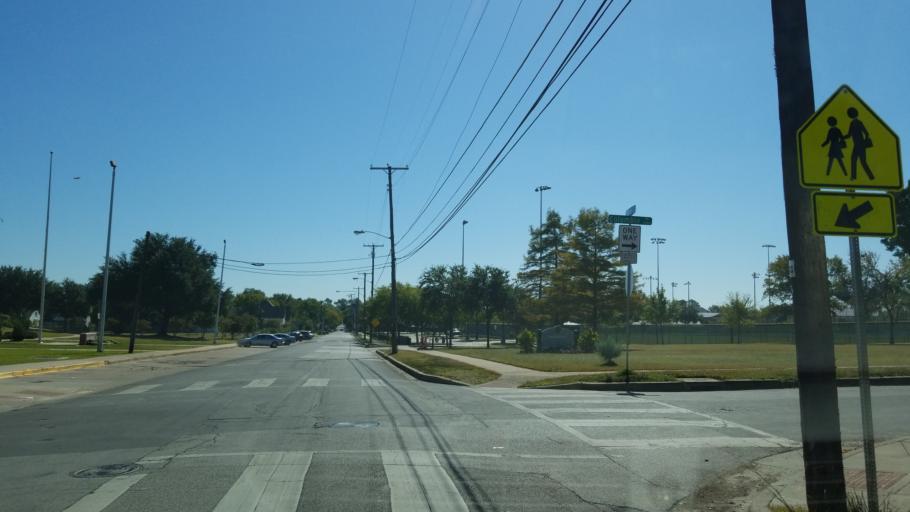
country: US
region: Texas
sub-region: Dallas County
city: Highland Park
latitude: 32.8056
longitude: -96.7516
